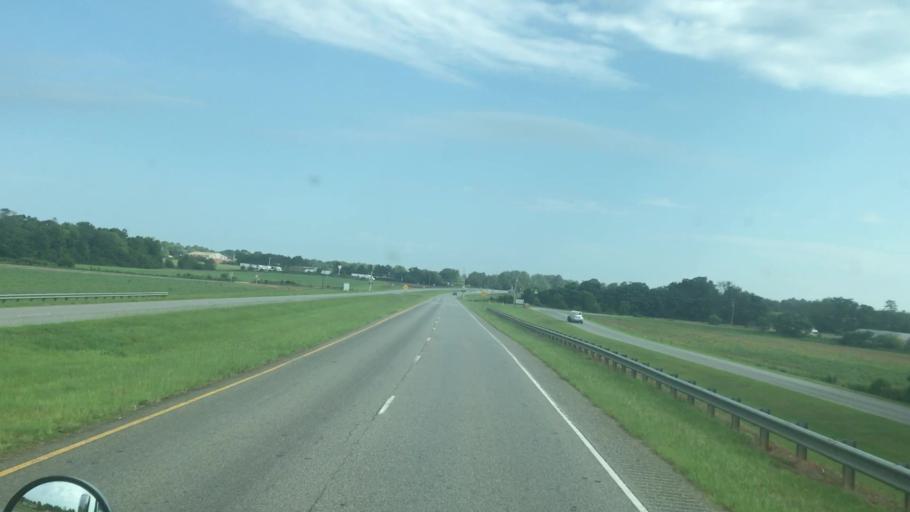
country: US
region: Georgia
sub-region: Early County
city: Blakely
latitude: 31.3856
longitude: -84.9220
